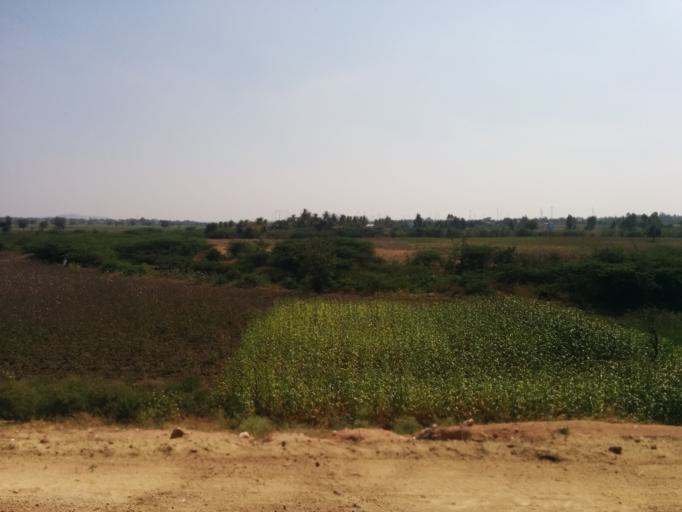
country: IN
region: Karnataka
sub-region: Gadag
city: Gadag
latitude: 15.4381
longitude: 75.5444
